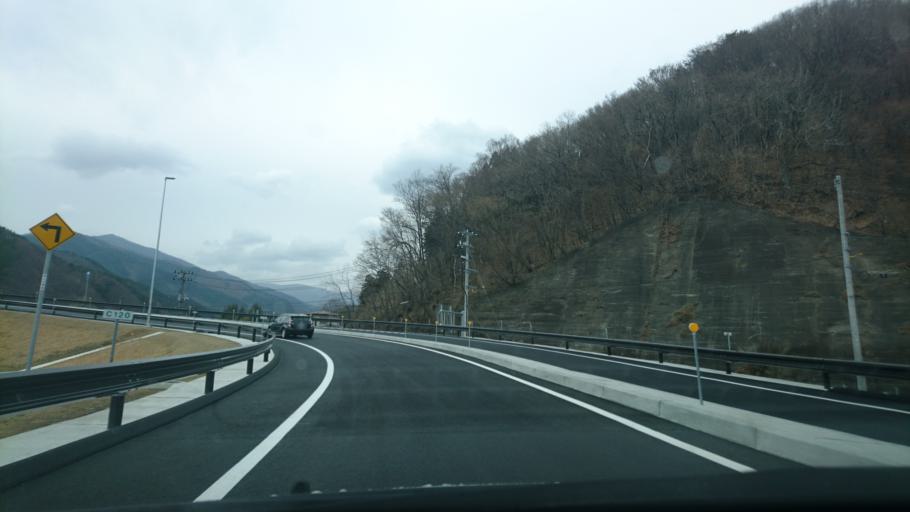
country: JP
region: Iwate
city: Kamaishi
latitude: 39.2654
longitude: 141.8433
